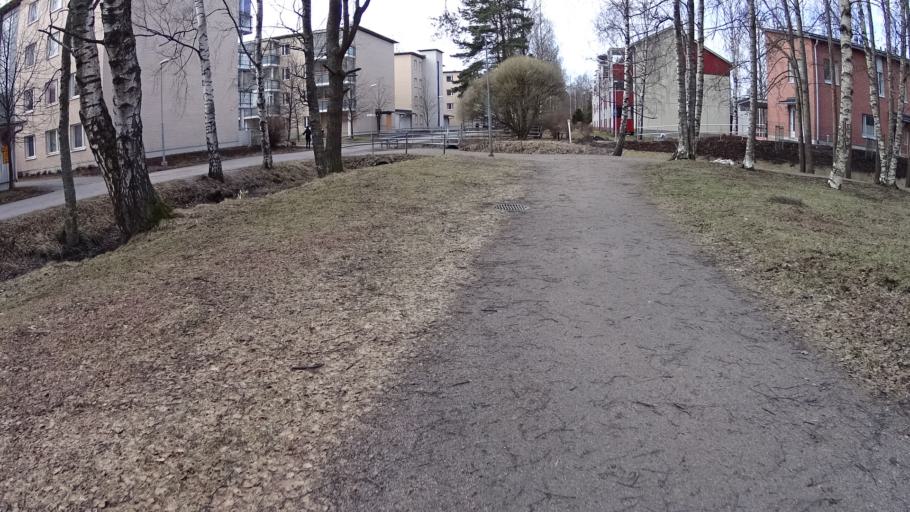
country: FI
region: Uusimaa
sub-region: Helsinki
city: Teekkarikylae
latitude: 60.2312
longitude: 24.8771
